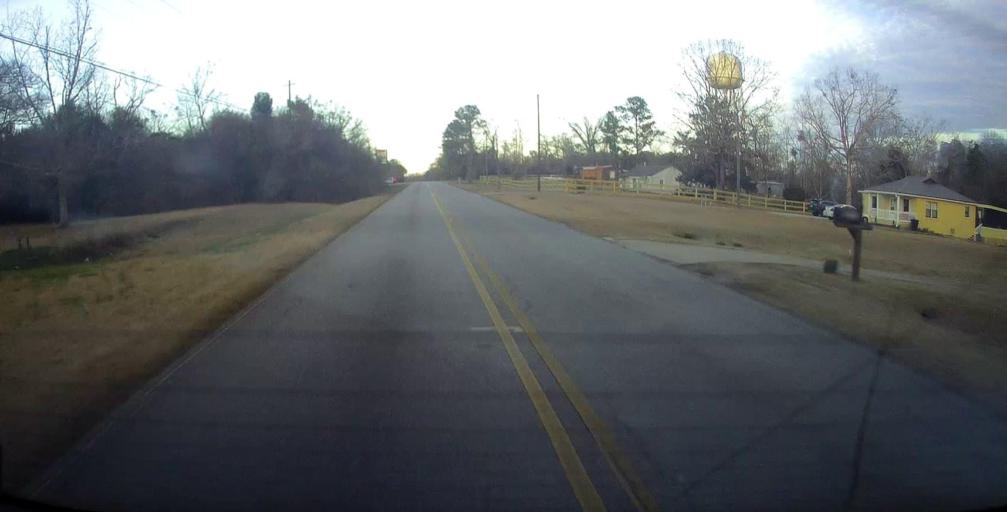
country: US
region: Georgia
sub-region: Harris County
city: Hamilton
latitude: 32.6204
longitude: -84.8175
